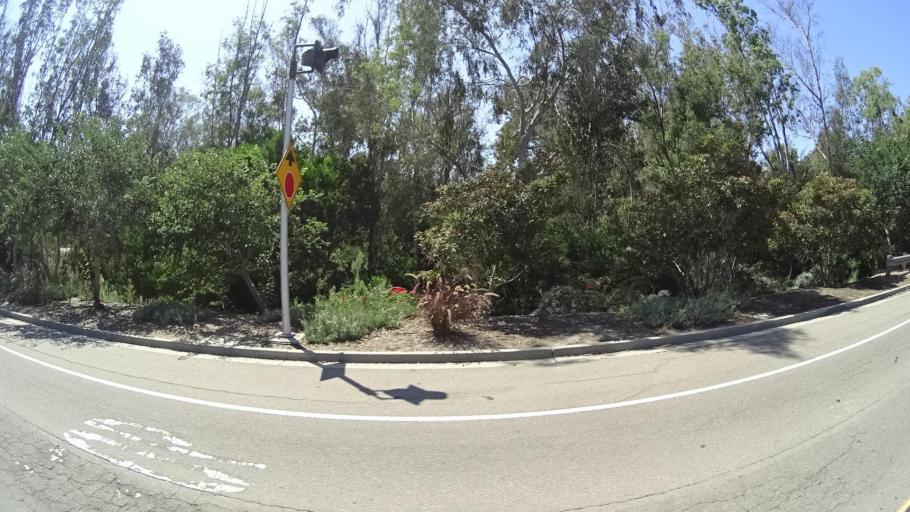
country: US
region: California
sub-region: San Diego County
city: Fairbanks Ranch
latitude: 32.9770
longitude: -117.1807
